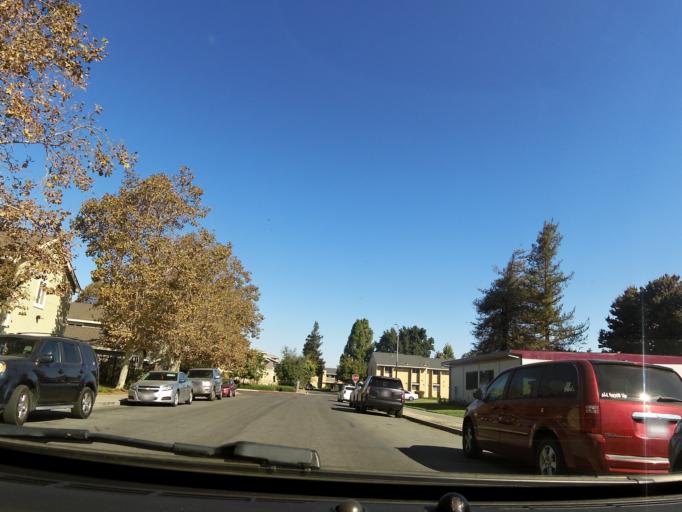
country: US
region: California
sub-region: San Benito County
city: Hollister
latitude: 36.8428
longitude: -121.3968
